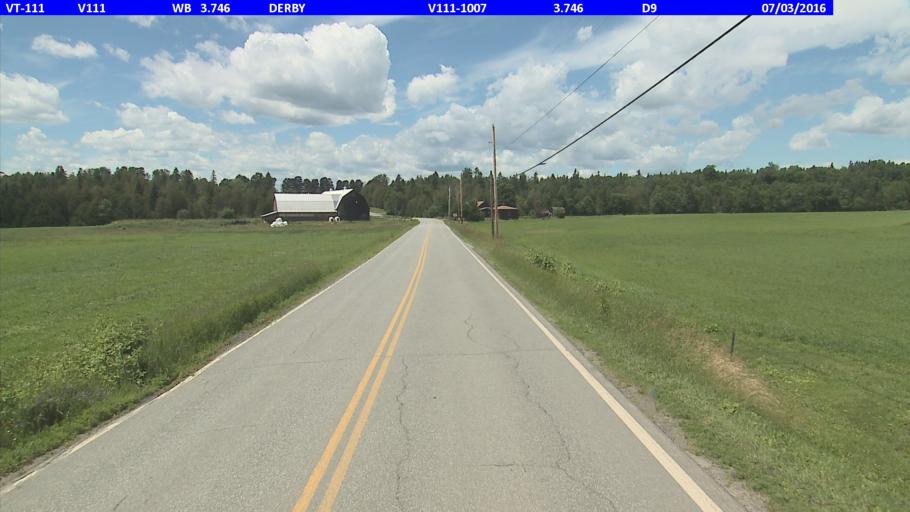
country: US
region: Vermont
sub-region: Orleans County
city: Newport
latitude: 44.9327
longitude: -72.0660
